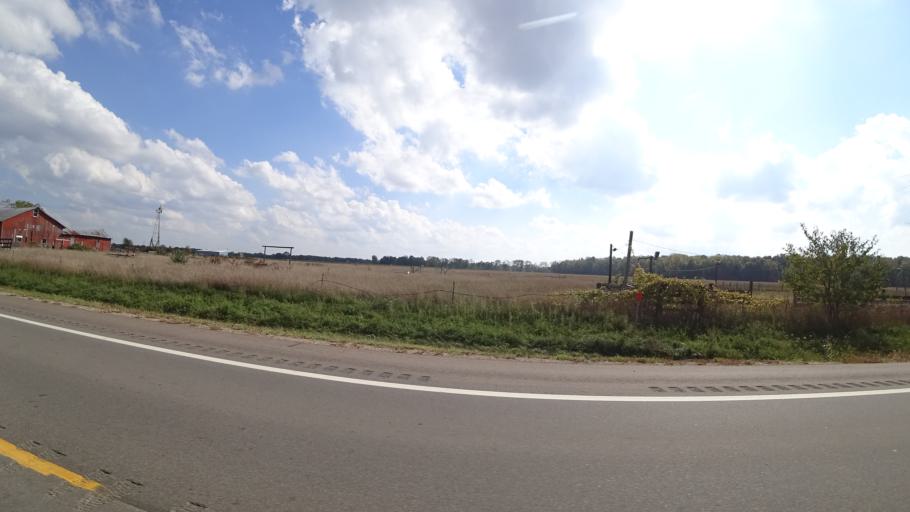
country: US
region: Michigan
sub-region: Calhoun County
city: Athens
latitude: 42.0633
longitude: -85.1997
